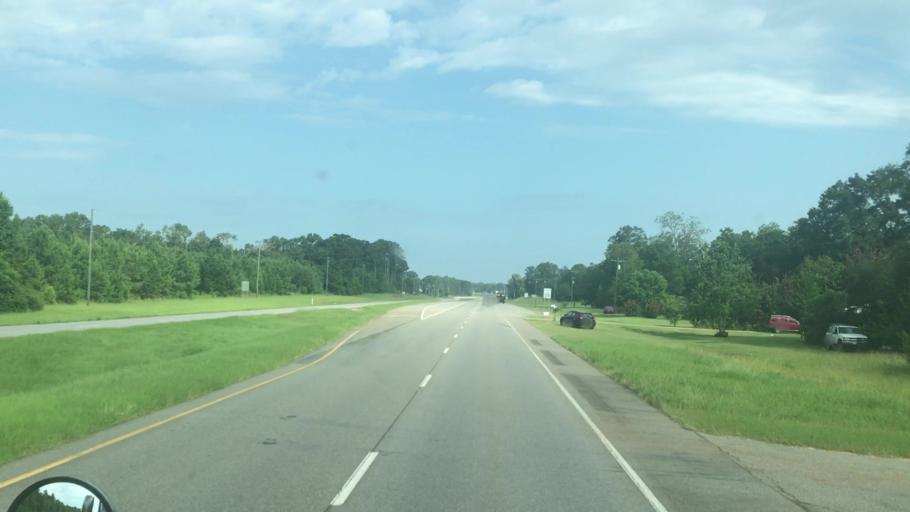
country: US
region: Georgia
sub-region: Early County
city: Blakely
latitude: 31.3487
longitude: -84.9144
